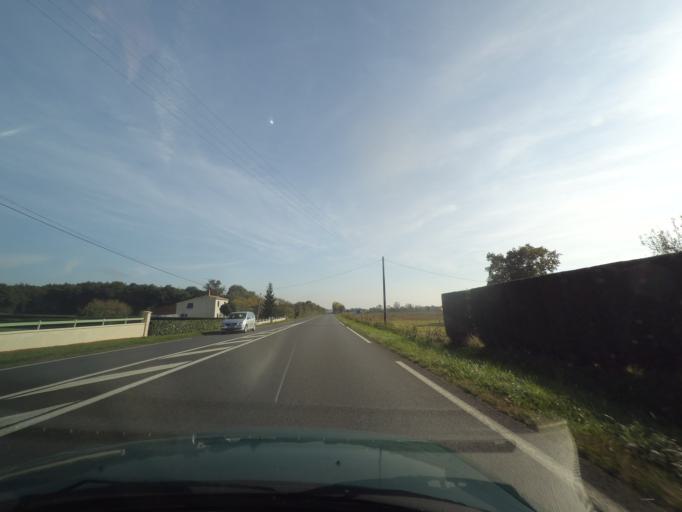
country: FR
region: Pays de la Loire
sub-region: Departement de Maine-et-Loire
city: Vihiers
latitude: 47.1503
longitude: -0.4743
